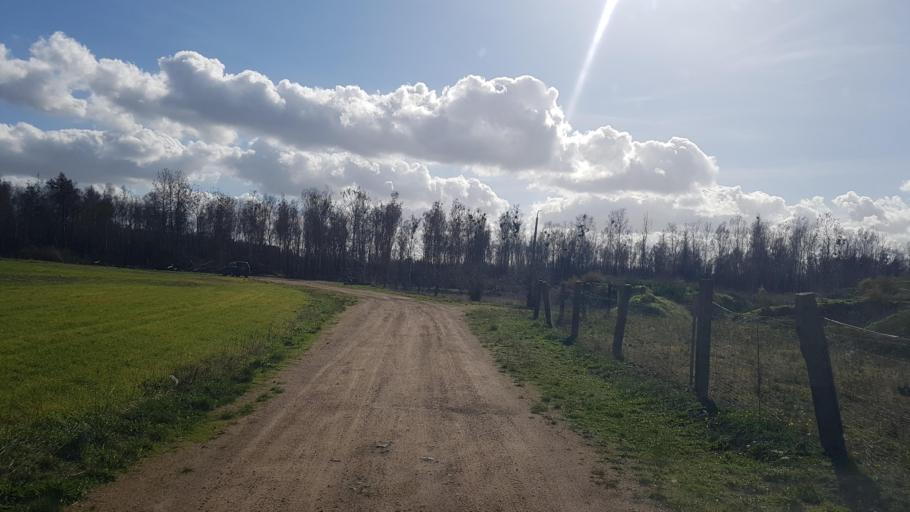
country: DE
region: Brandenburg
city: Muhlberg
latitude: 51.4378
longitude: 13.3072
